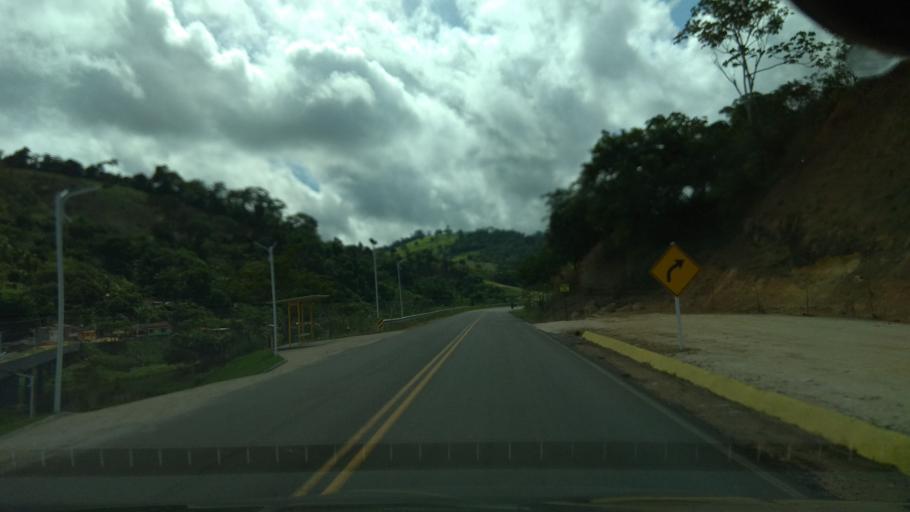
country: BR
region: Bahia
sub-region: Mutuipe
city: Mutuipe
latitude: -13.1843
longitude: -39.4403
